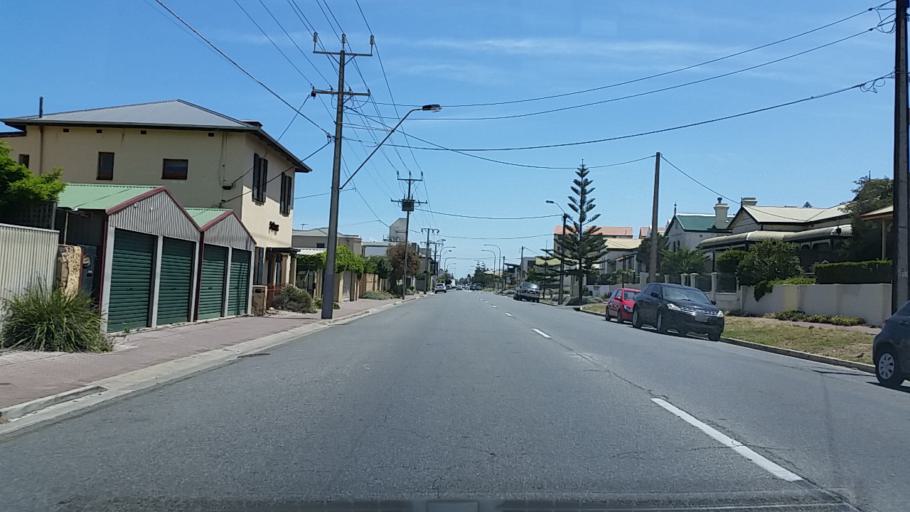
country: AU
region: South Australia
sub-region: Charles Sturt
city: Henley Beach
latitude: -34.9240
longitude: 138.4955
